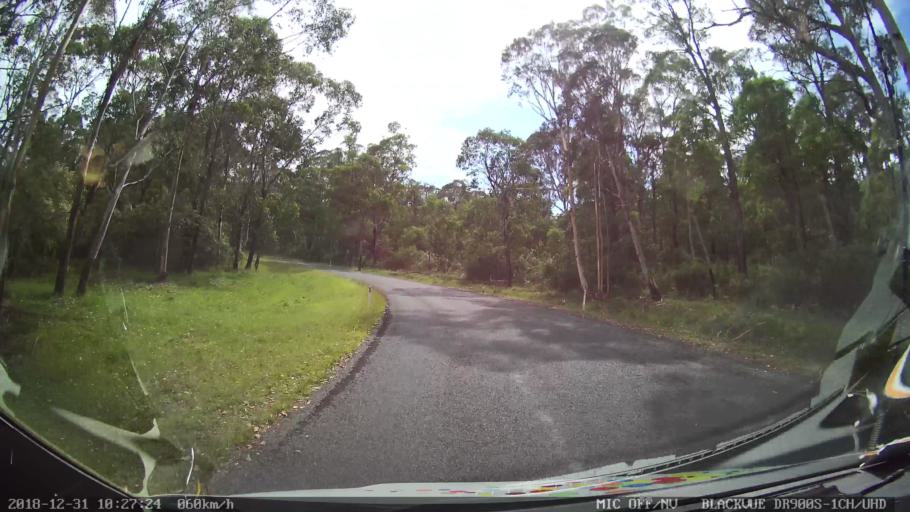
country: AU
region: New South Wales
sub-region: Snowy River
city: Jindabyne
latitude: -36.4869
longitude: 148.1440
